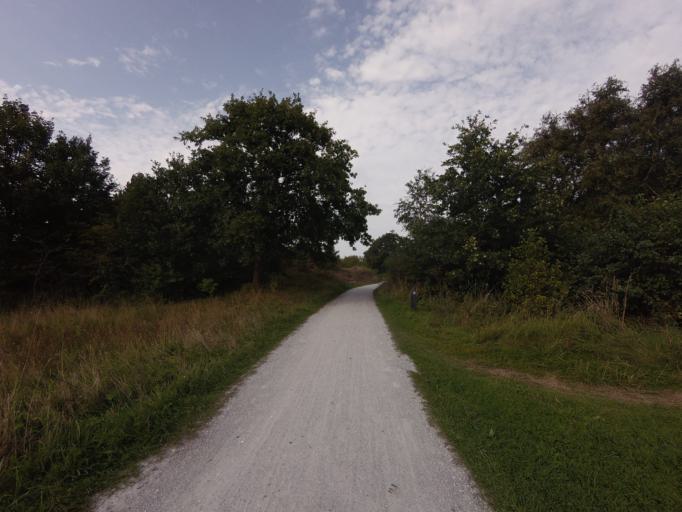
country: NL
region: Friesland
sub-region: Gemeente Schiermonnikoog
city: Schiermonnikoog
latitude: 53.4837
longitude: 6.1595
